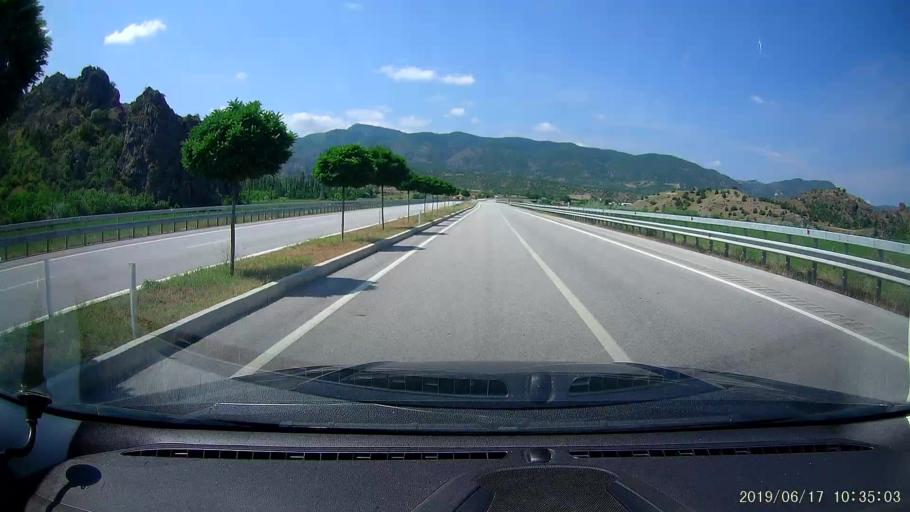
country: TR
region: Corum
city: Osmancik
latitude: 40.9782
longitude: 34.7115
